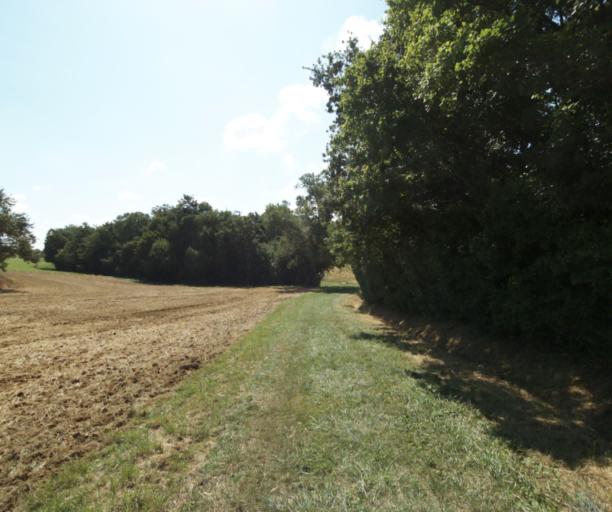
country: FR
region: Midi-Pyrenees
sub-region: Departement de la Haute-Garonne
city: Auriac-sur-Vendinelle
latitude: 43.4590
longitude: 1.7897
